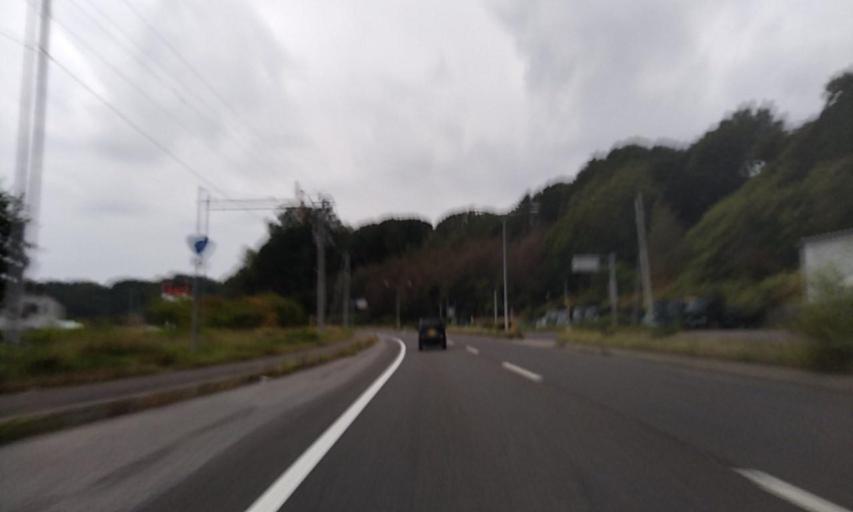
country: JP
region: Hokkaido
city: Abashiri
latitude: 44.0165
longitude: 144.2825
